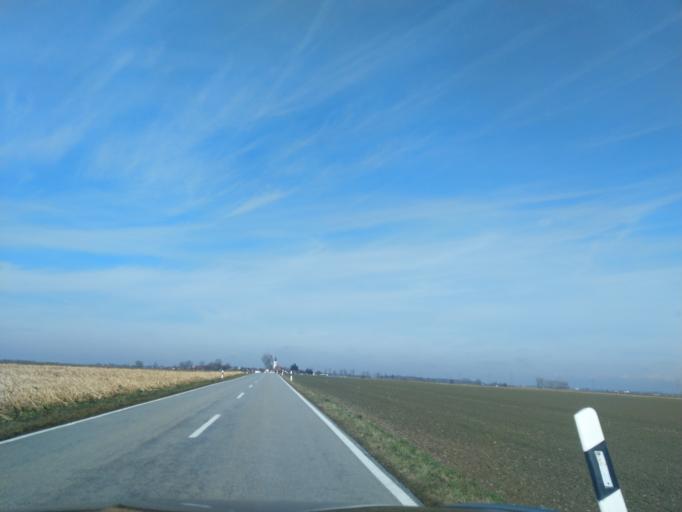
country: DE
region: Bavaria
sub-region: Lower Bavaria
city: Buchhofen
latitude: 48.6800
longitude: 12.9594
